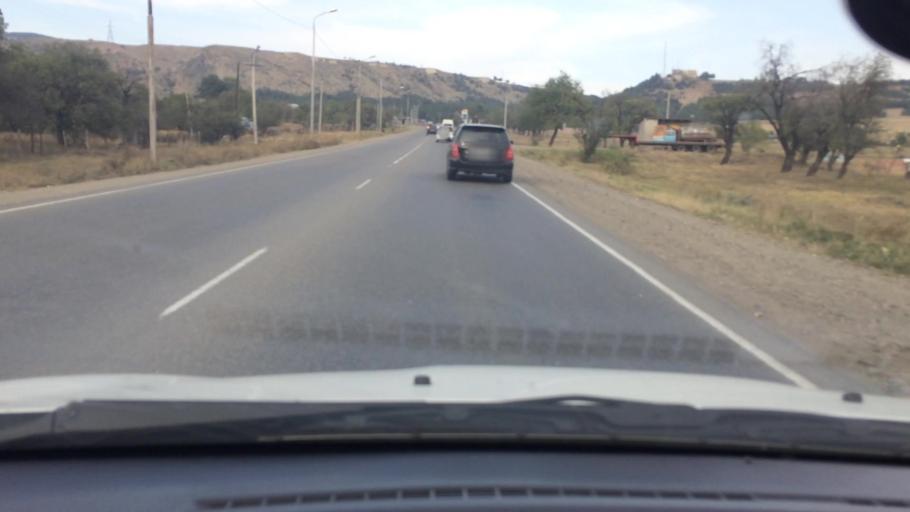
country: GE
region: T'bilisi
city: Tbilisi
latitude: 41.6152
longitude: 44.7910
